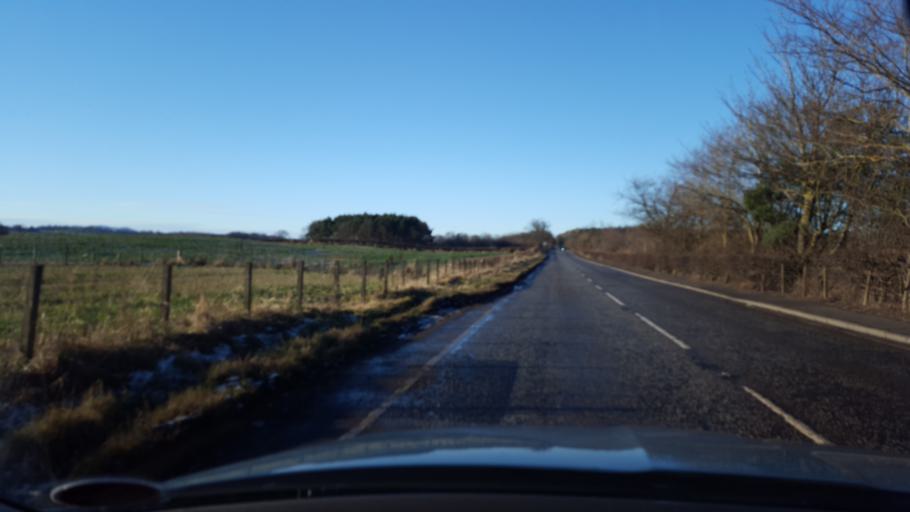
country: GB
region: Scotland
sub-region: West Lothian
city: Broxburn
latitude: 55.9620
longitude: -3.4836
